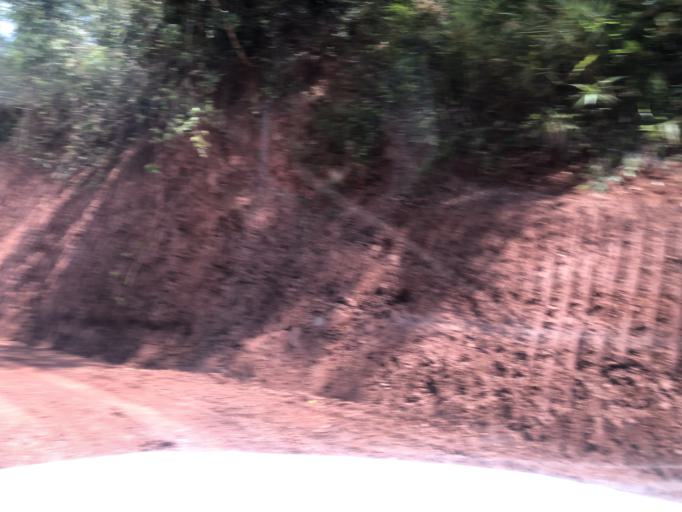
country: CN
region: Yunnan
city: Menglie
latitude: 22.2381
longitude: 101.6168
